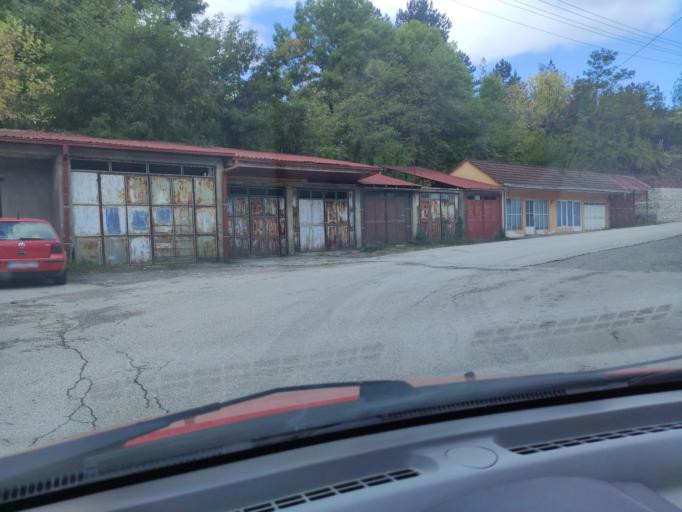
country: MK
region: Kratovo
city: Kratovo
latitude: 42.0788
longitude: 22.1711
